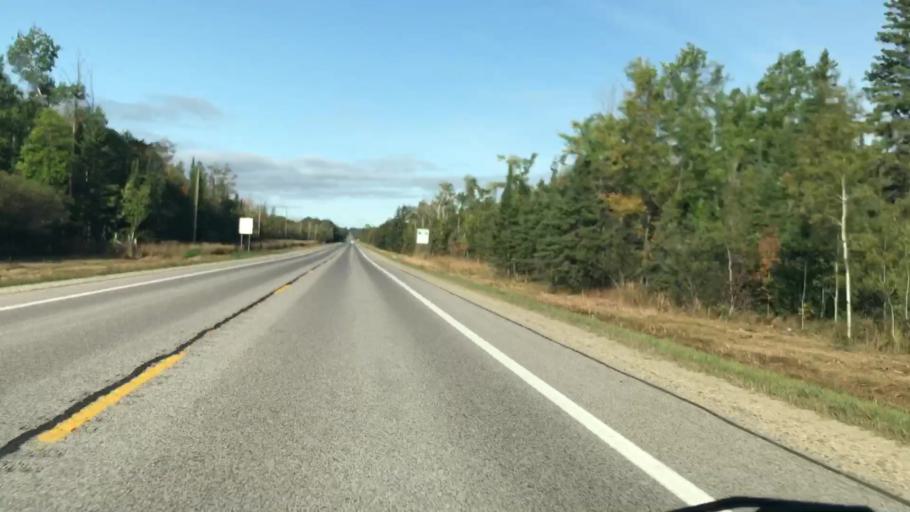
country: US
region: Michigan
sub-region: Luce County
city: Newberry
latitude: 46.3035
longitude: -85.3782
